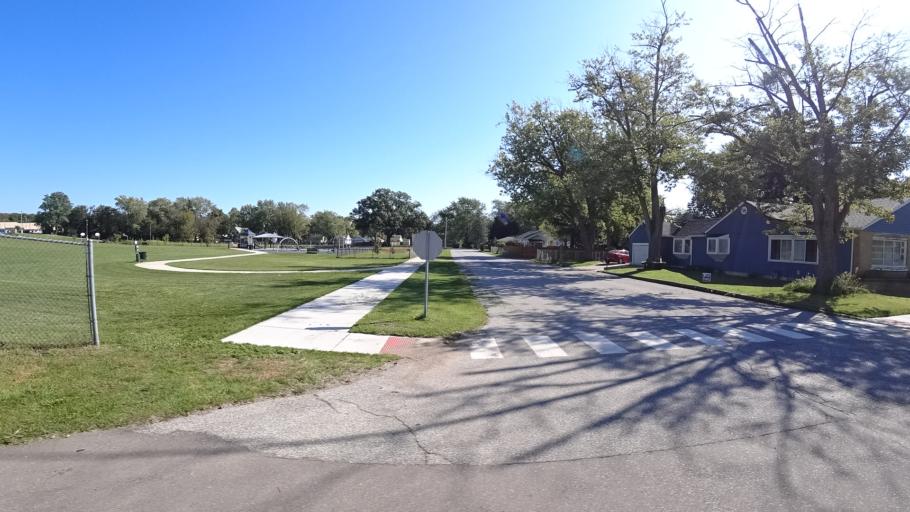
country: US
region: Indiana
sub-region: LaPorte County
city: Michigan City
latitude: 41.7097
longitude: -86.8846
